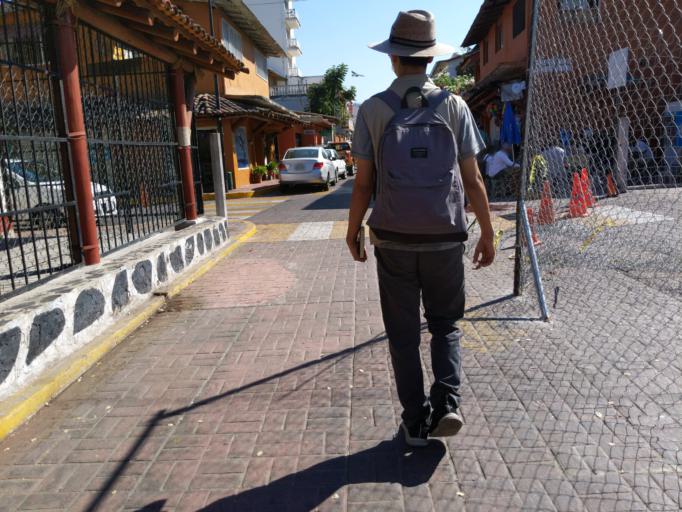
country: MX
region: Guerrero
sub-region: Zihuatanejo de Azueta
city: Ixtapa-Zihuatanejo
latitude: 17.6374
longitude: -101.5598
